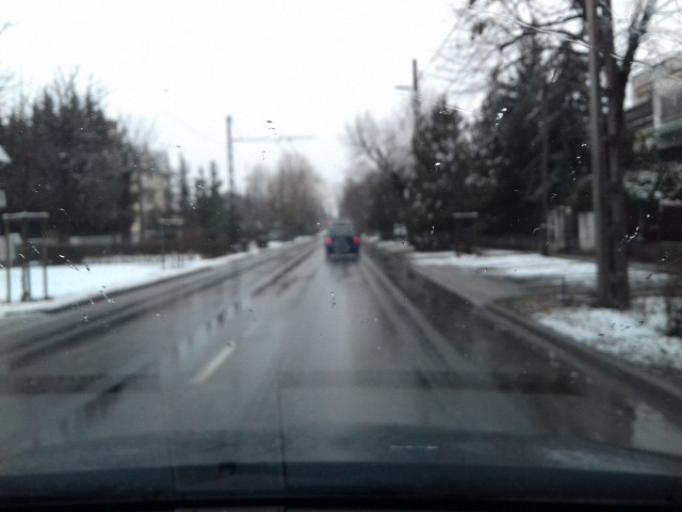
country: HU
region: Budapest
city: Budapest XIV. keruelet
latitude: 47.5222
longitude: 19.1376
